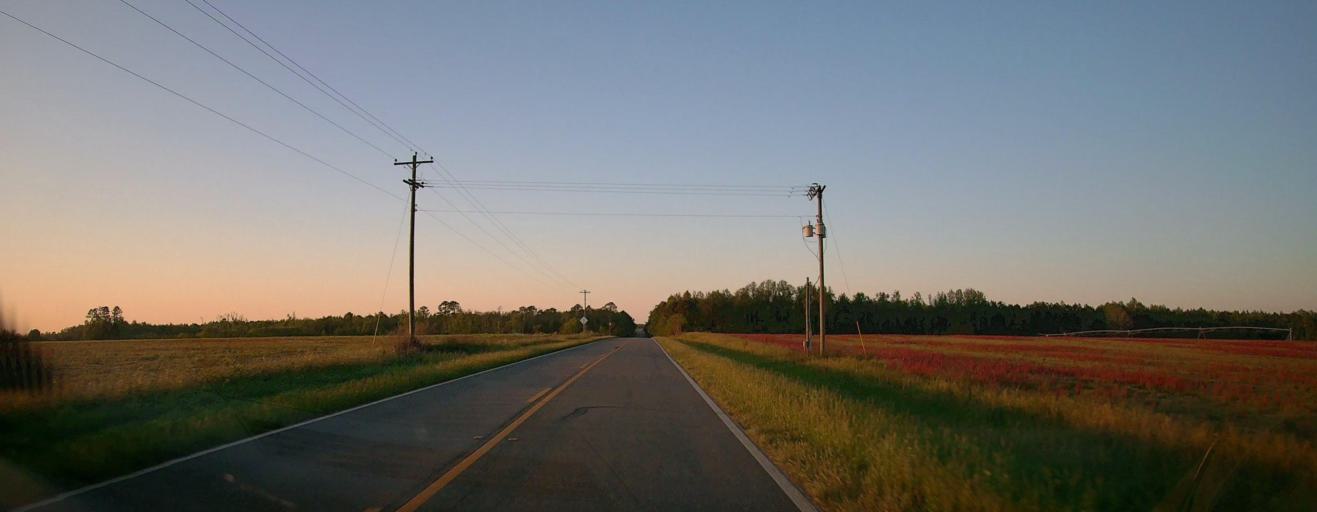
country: US
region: Georgia
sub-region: Ben Hill County
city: Fitzgerald
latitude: 31.7318
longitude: -83.3098
